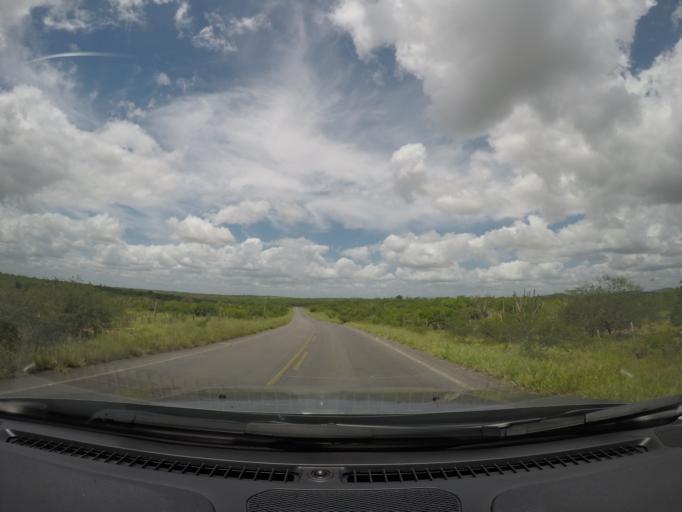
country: BR
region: Bahia
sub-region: Ipira
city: Ipira
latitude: -12.2879
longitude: -39.8713
